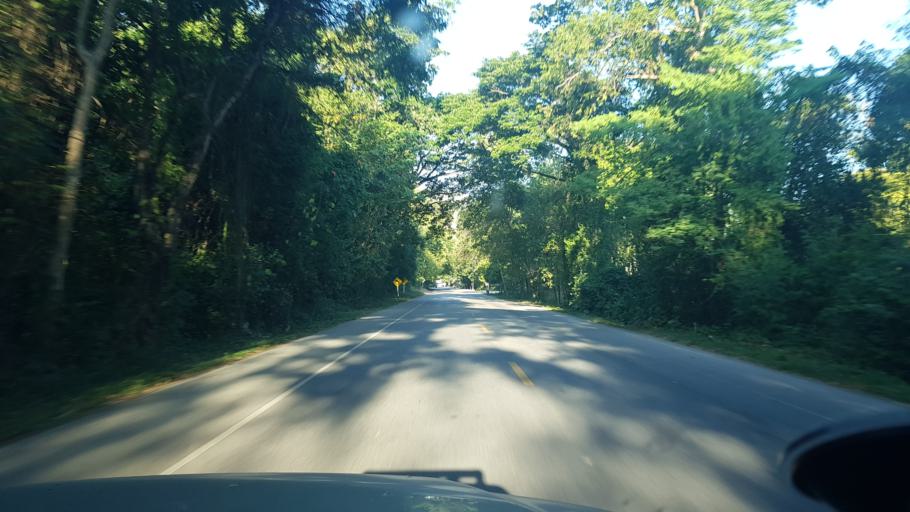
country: TH
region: Khon Kaen
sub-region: Amphoe Phu Pha Man
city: Phu Pha Man
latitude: 16.6482
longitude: 101.8134
